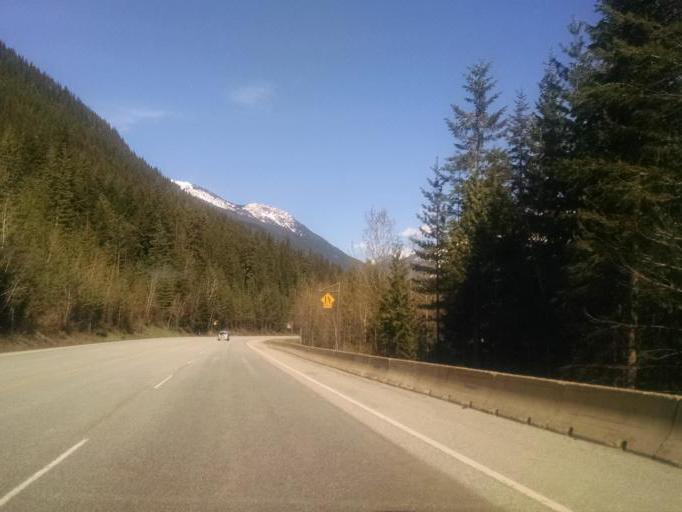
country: CA
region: British Columbia
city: Revelstoke
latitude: 51.0205
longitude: -118.0664
